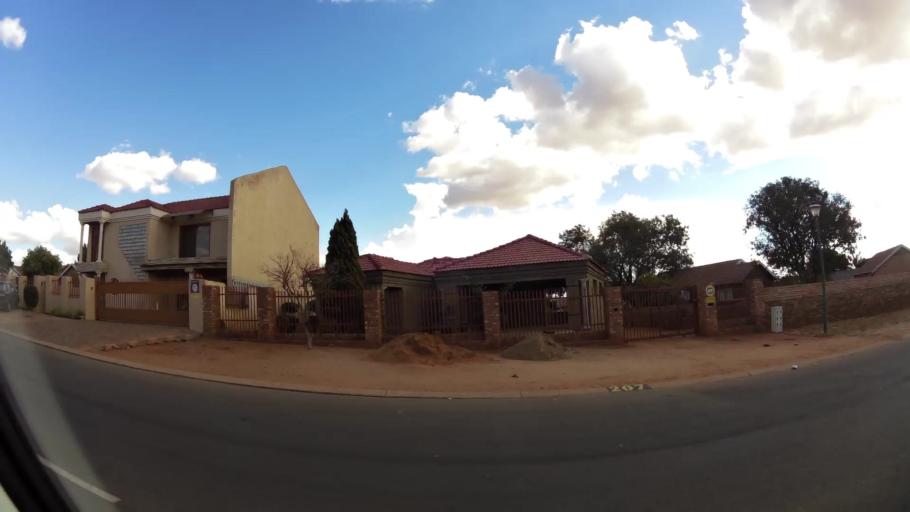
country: ZA
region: Limpopo
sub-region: Capricorn District Municipality
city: Polokwane
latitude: -23.9057
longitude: 29.5002
